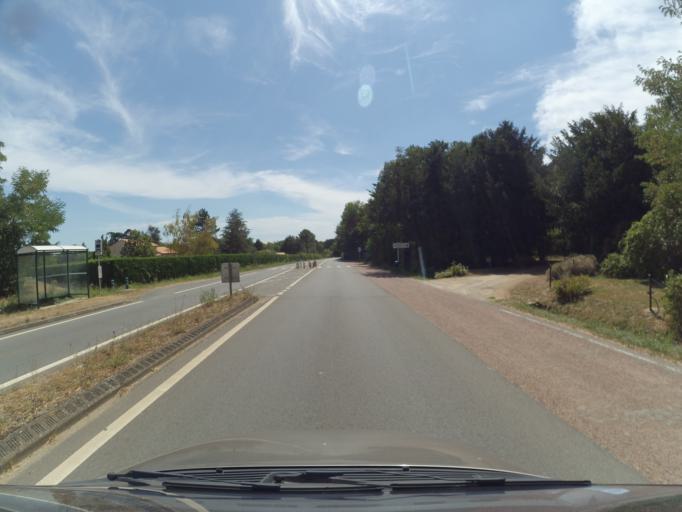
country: FR
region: Poitou-Charentes
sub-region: Departement de la Vienne
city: Saint-Maurice-la-Clouere
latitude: 46.3816
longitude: 0.4026
